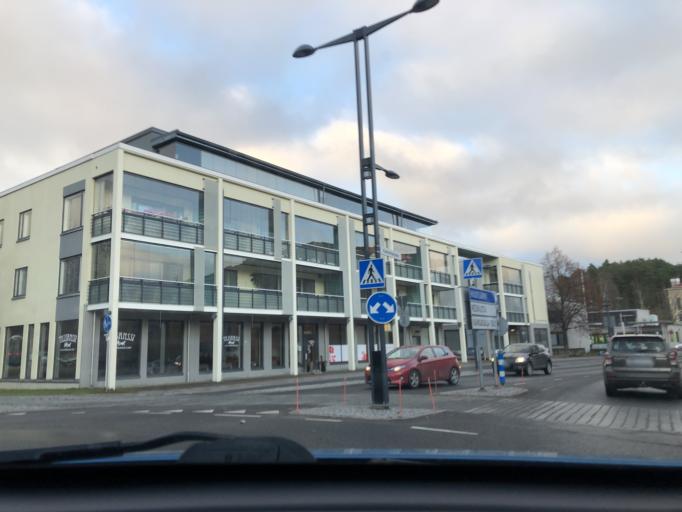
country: FI
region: Pirkanmaa
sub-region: Tampere
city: Kangasala
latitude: 61.4637
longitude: 24.0718
